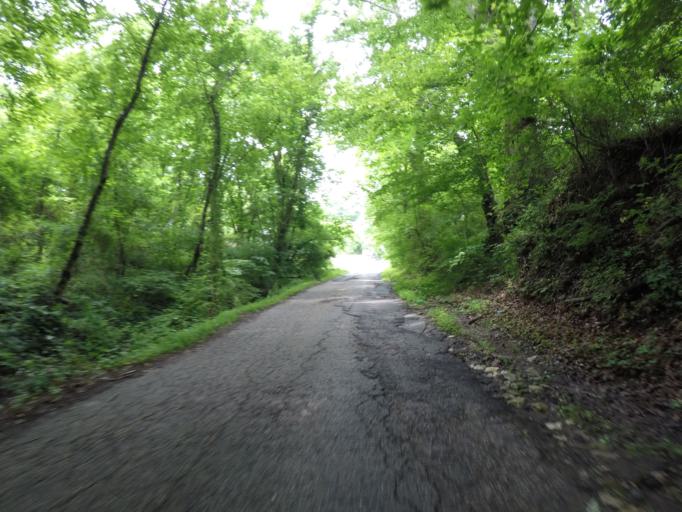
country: US
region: West Virginia
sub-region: Cabell County
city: Huntington
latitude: 38.4144
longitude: -82.3966
